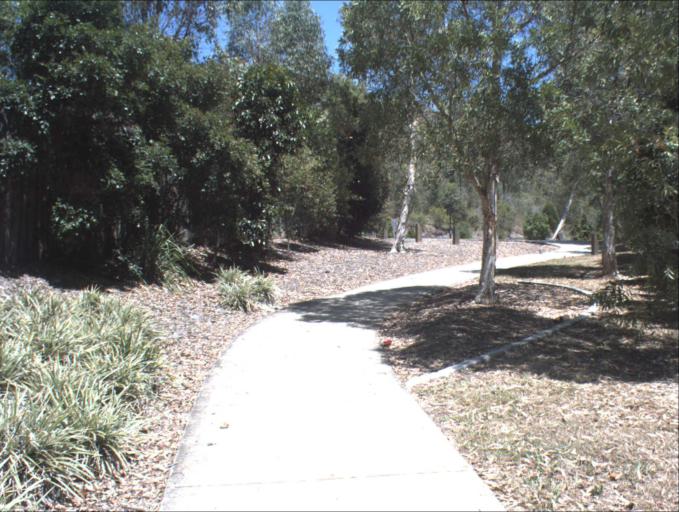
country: AU
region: Queensland
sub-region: Logan
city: Windaroo
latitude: -27.7474
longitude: 153.1859
